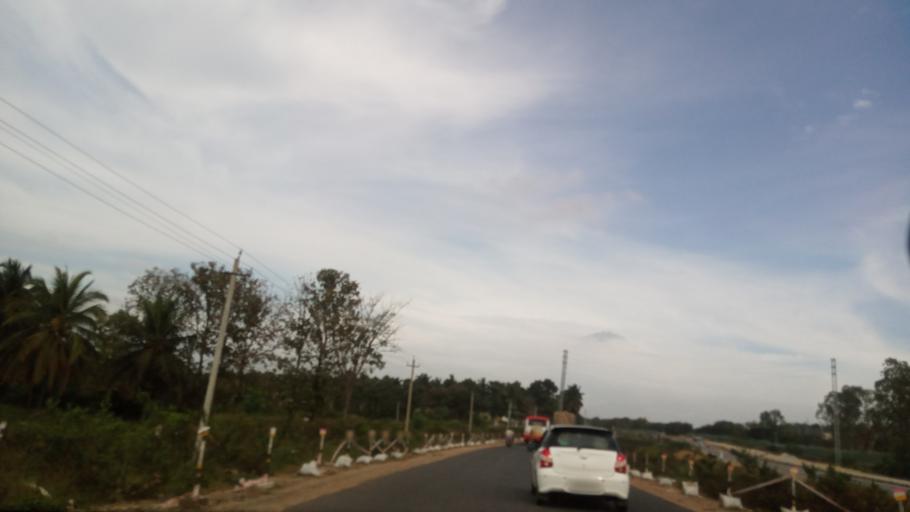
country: IN
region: Karnataka
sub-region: Mandya
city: Shrirangapattana
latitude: 12.4409
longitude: 76.7249
